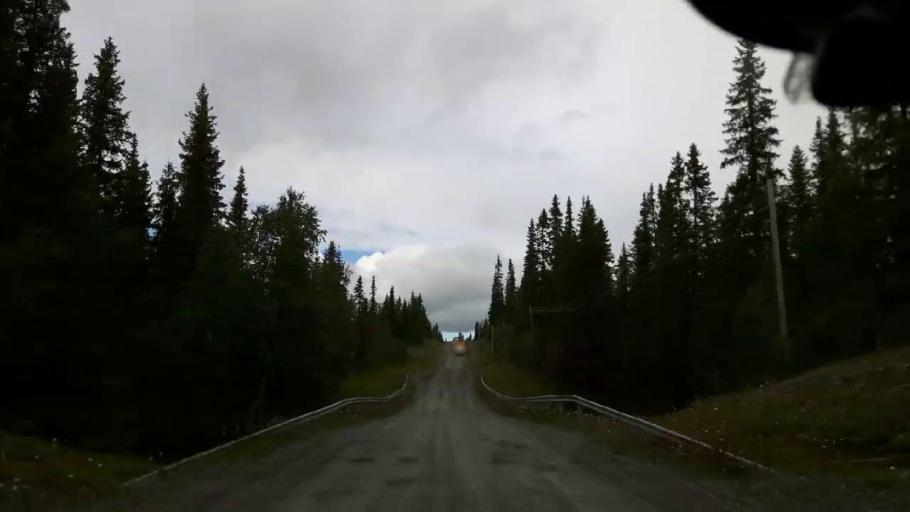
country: SE
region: Jaemtland
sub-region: Krokoms Kommun
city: Valla
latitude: 63.7230
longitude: 13.8496
